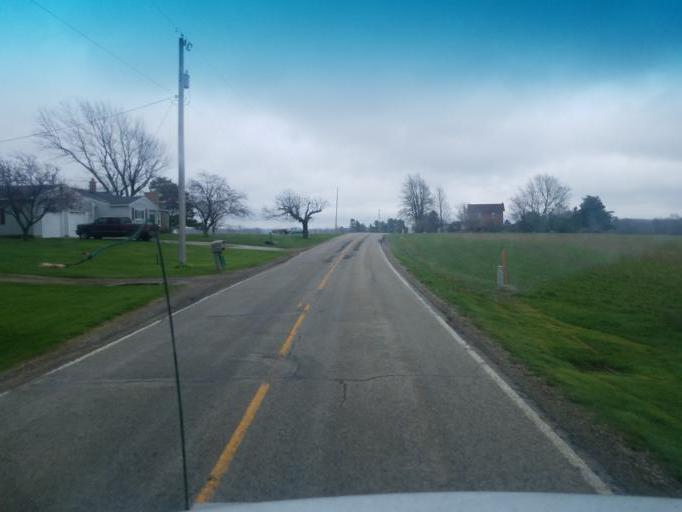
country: US
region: Ohio
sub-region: Richland County
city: Shelby
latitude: 40.9082
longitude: -82.6280
